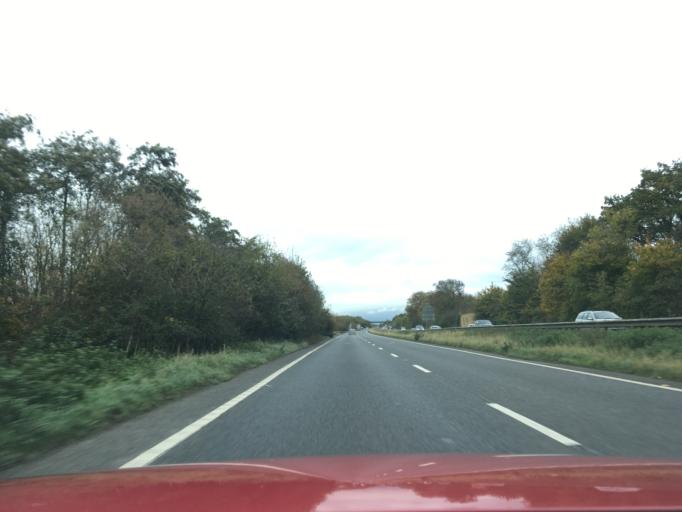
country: GB
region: England
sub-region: Somerset
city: Stoke-sub-Hamdon
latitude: 50.9706
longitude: -2.7369
